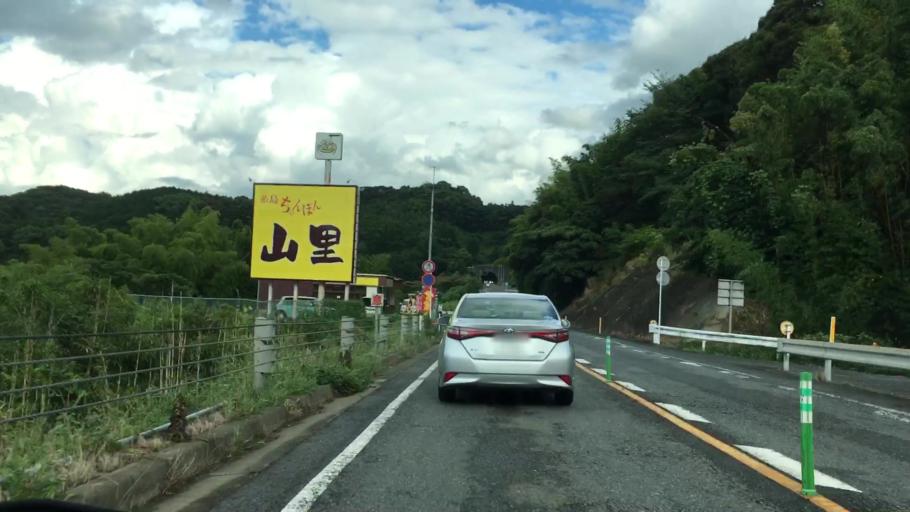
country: JP
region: Fukuoka
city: Maebaru-chuo
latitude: 33.5041
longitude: 130.1018
